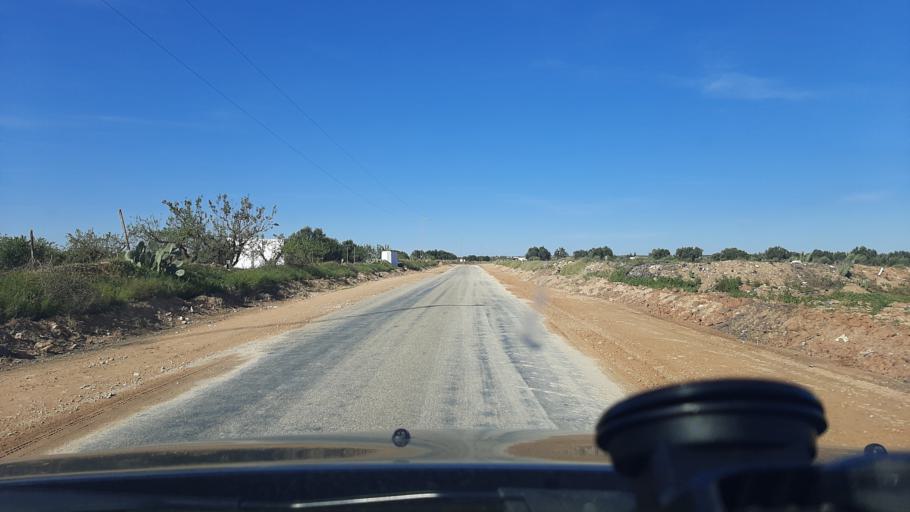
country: TN
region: Safaqis
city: Sfax
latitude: 34.9179
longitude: 10.5831
